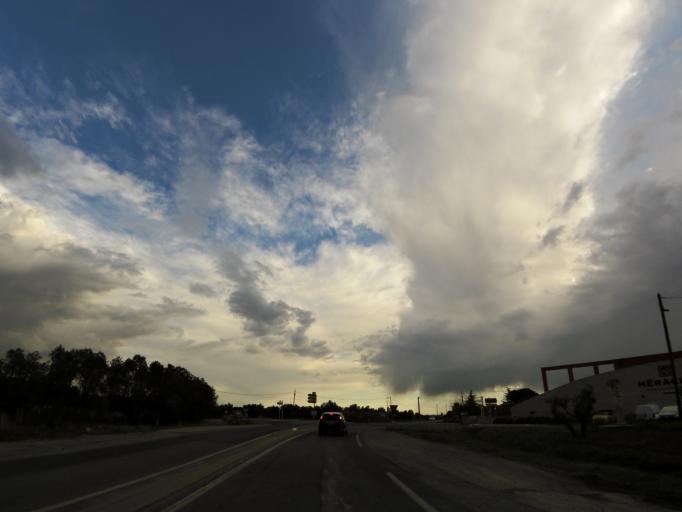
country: FR
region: Languedoc-Roussillon
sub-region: Departement du Gard
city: Codognan
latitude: 43.7341
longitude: 4.2356
